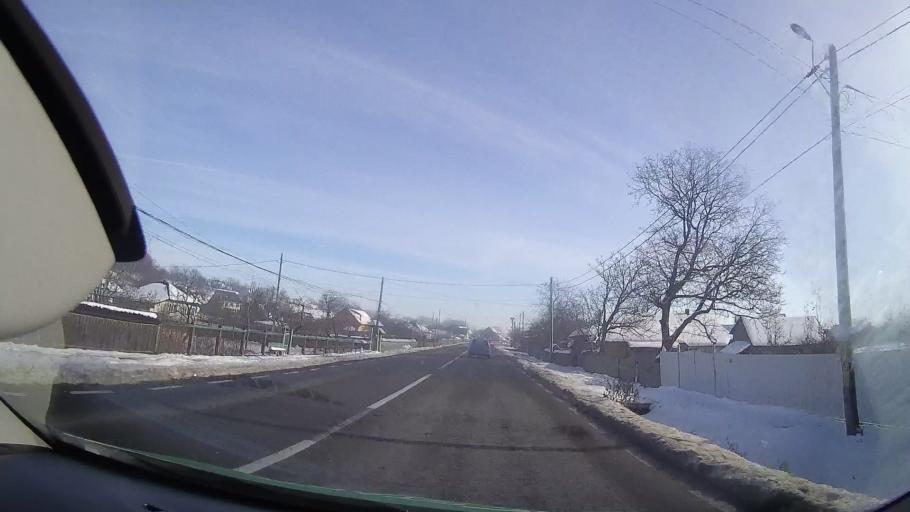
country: RO
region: Neamt
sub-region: Comuna Cracaoani
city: Cracaoani
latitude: 47.0886
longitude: 26.3277
